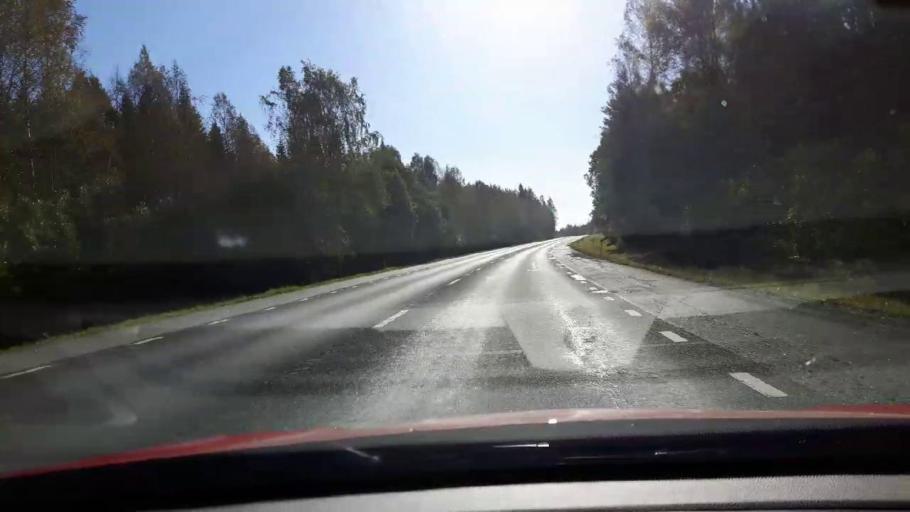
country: SE
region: Jaemtland
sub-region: Braecke Kommun
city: Braecke
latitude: 62.6950
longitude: 15.5345
